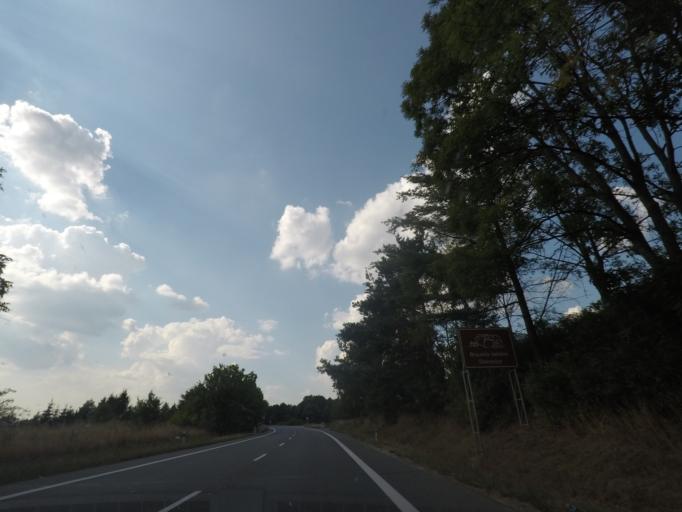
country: CZ
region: Kralovehradecky
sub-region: Okres Nachod
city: Jaromer
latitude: 50.3994
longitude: 15.8968
